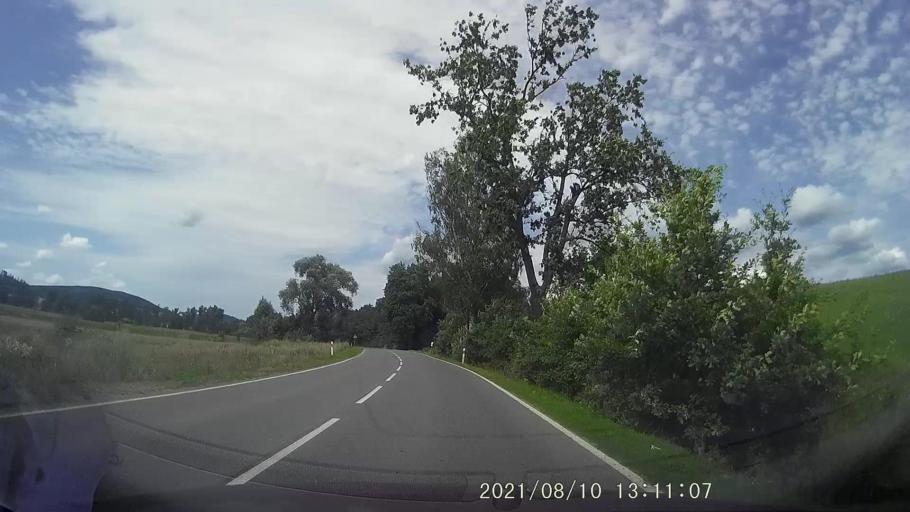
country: PL
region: Lower Silesian Voivodeship
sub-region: Powiat klodzki
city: Bozkow
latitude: 50.5058
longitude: 16.5238
